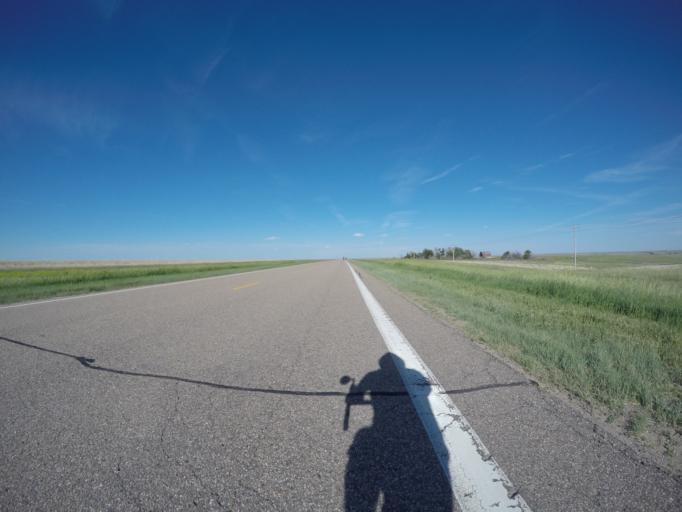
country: US
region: Kansas
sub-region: Cheyenne County
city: Saint Francis
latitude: 39.7568
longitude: -101.9322
